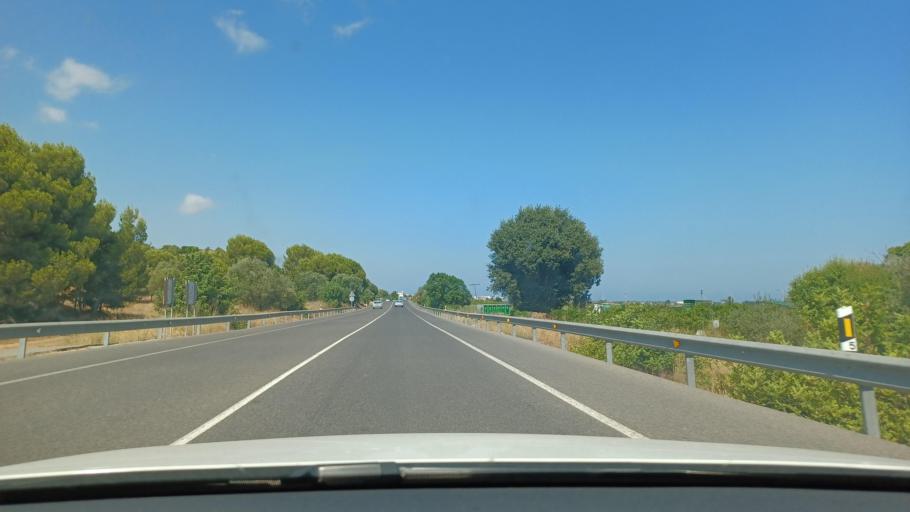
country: ES
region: Valencia
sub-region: Provincia de Castello
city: Chilches
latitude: 39.7723
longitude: -0.2060
